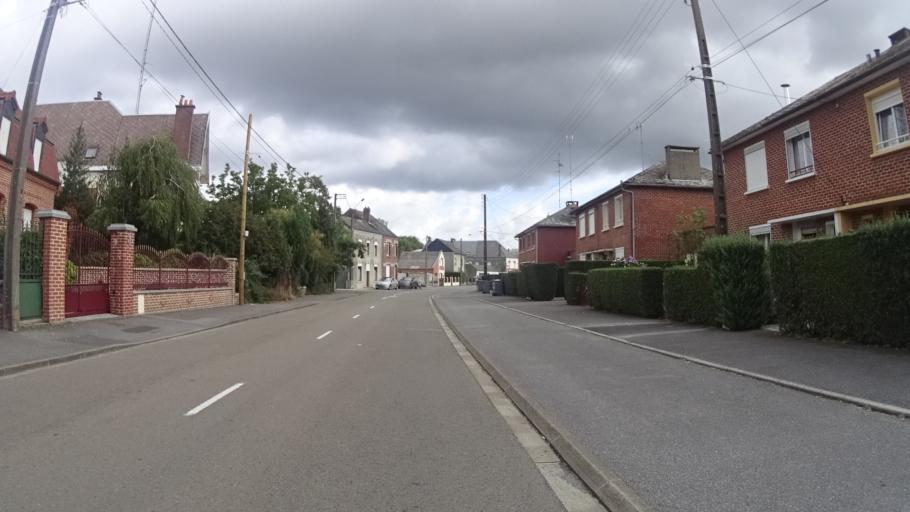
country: FR
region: Nord-Pas-de-Calais
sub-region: Departement du Nord
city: Landrecies
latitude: 50.1215
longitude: 3.6921
